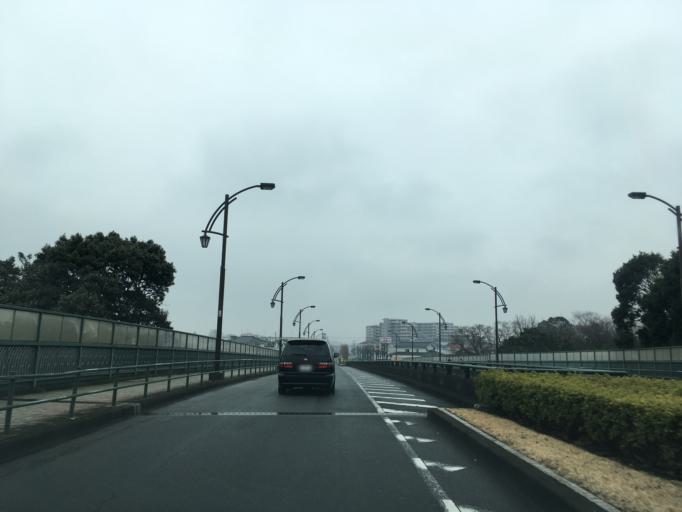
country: JP
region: Tokyo
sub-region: Machida-shi
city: Machida
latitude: 35.5737
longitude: 139.4256
